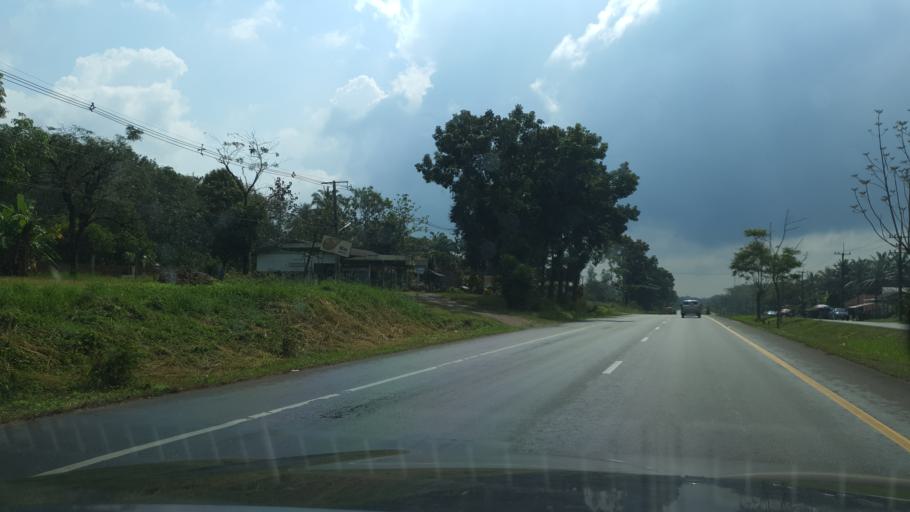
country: TH
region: Chumphon
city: Tha Sae
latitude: 10.7690
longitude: 99.1956
